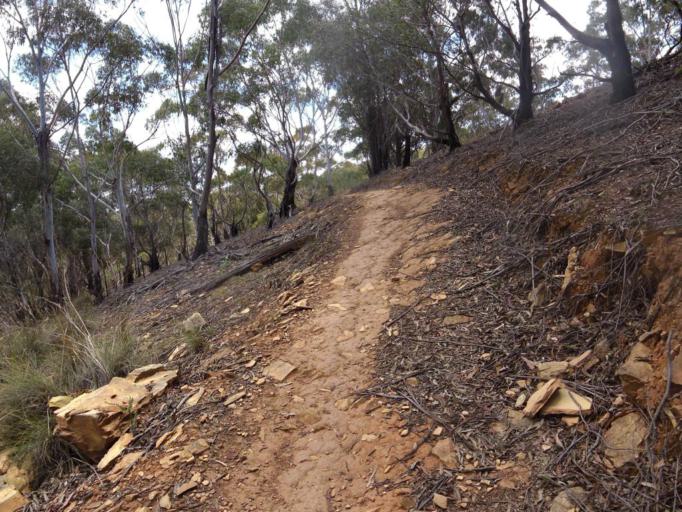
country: AU
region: Australian Capital Territory
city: Kaleen
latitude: -35.1382
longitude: 149.1400
